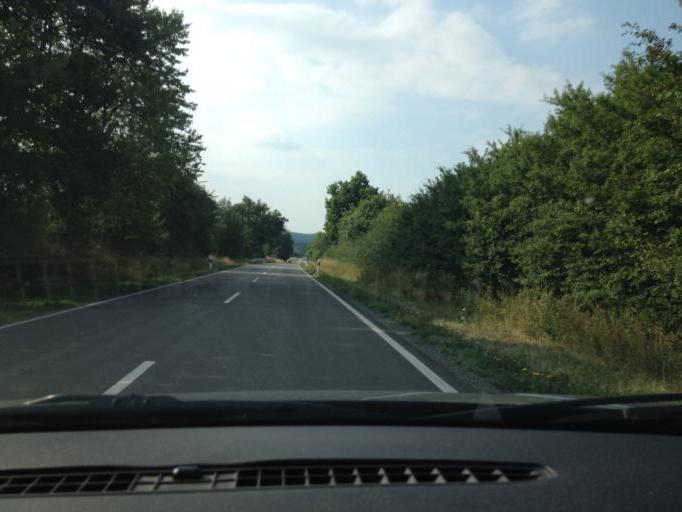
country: DE
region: Saarland
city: Nohfelden
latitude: 49.5656
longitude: 7.1232
